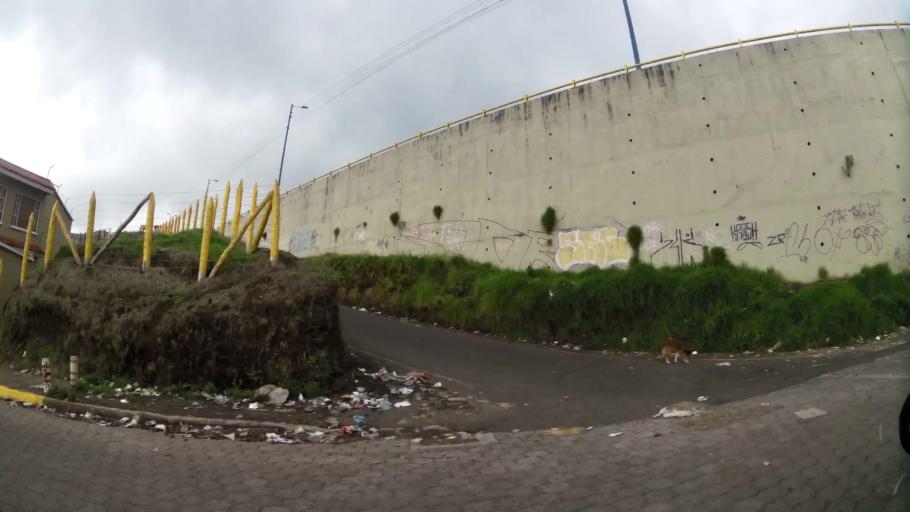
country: EC
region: Pichincha
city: Quito
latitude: -0.3036
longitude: -78.5218
